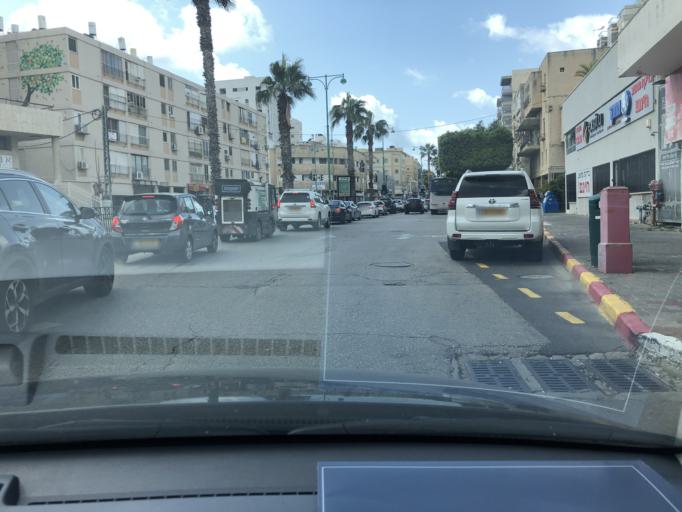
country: IL
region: Haifa
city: Hadera
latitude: 32.4380
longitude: 34.9269
